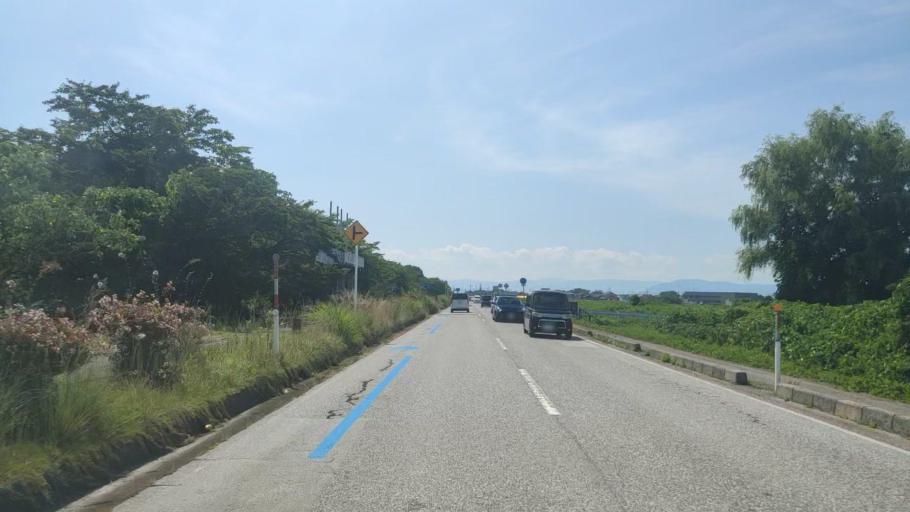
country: JP
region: Shiga Prefecture
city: Nagahama
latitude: 35.3883
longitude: 136.2298
